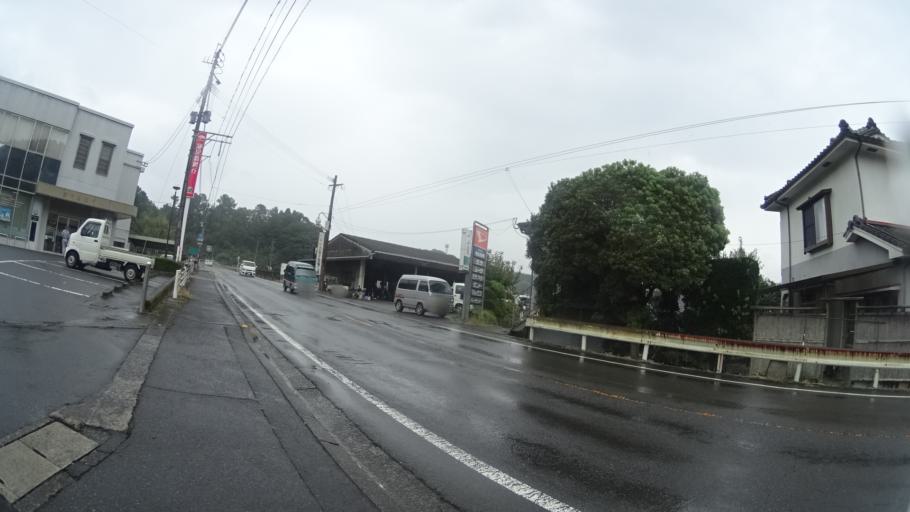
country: JP
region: Kagoshima
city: Kajiki
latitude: 31.9023
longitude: 130.6998
